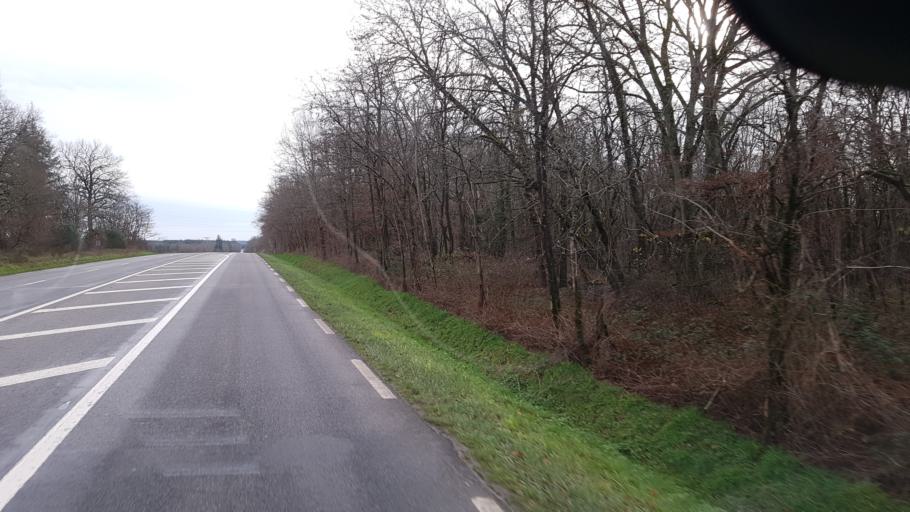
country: FR
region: Centre
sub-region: Departement du Loir-et-Cher
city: Nouan-le-Fuzelier
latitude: 47.5612
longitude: 2.0317
